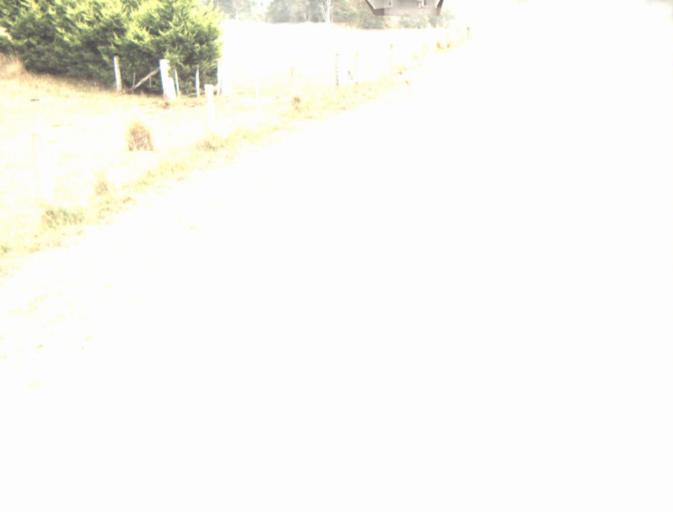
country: AU
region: Tasmania
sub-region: Dorset
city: Scottsdale
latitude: -41.3494
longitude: 147.4492
